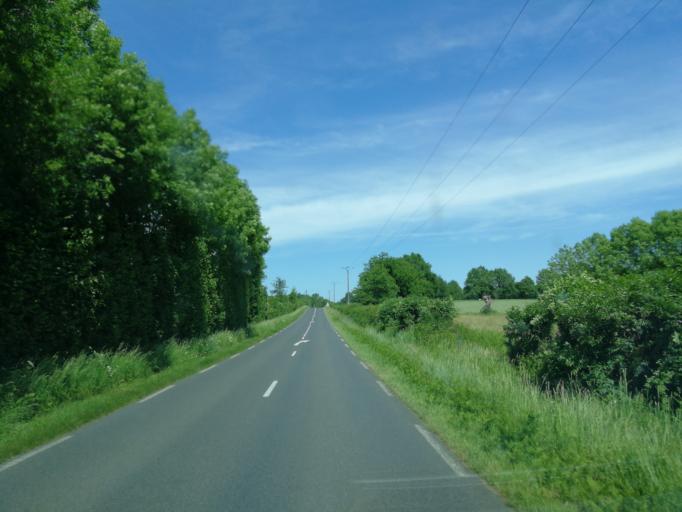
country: FR
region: Poitou-Charentes
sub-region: Departement des Deux-Sevres
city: Courlay
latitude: 46.8174
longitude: -0.5327
